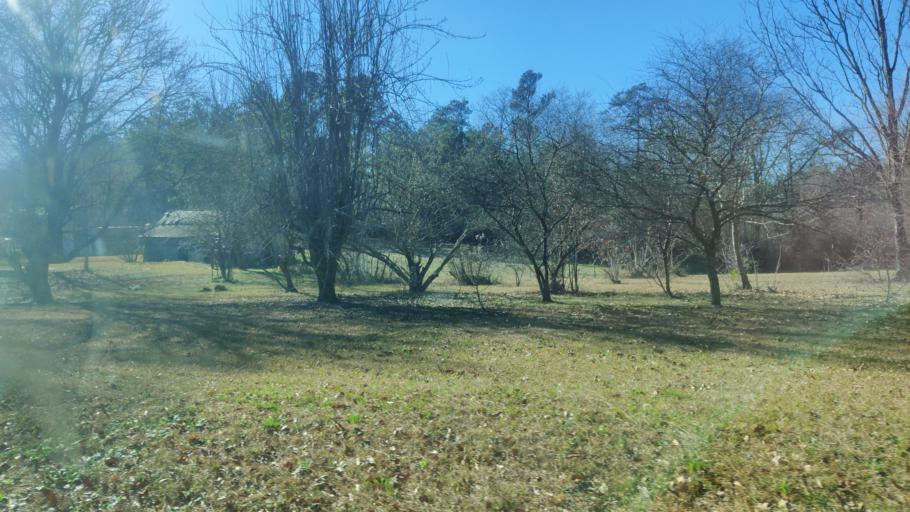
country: US
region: Mississippi
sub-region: Jones County
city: Ellisville
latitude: 31.5523
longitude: -89.3289
